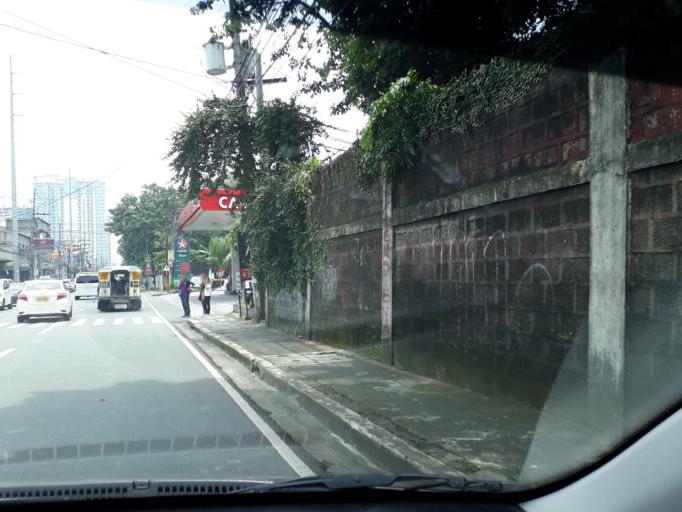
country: PH
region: Calabarzon
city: Del Monte
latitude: 14.6232
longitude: 121.0289
